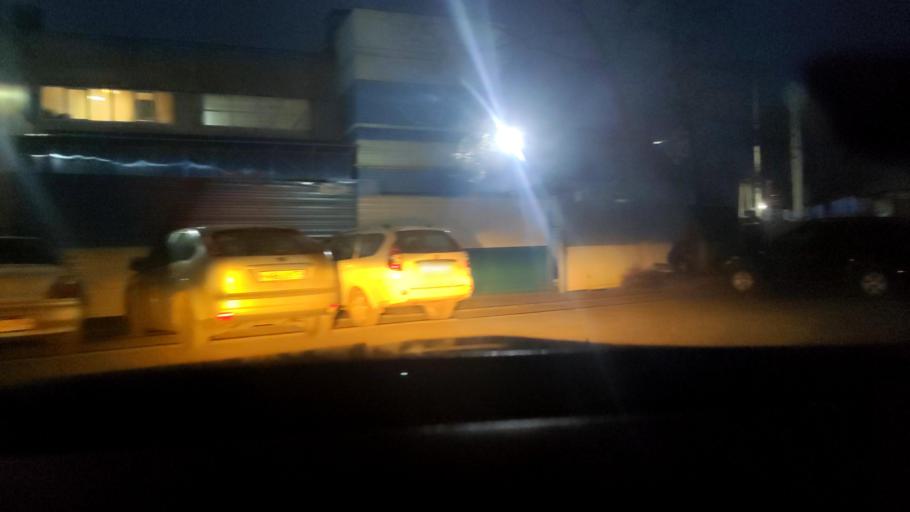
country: RU
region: Voronezj
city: Voronezh
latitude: 51.6820
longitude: 39.1502
